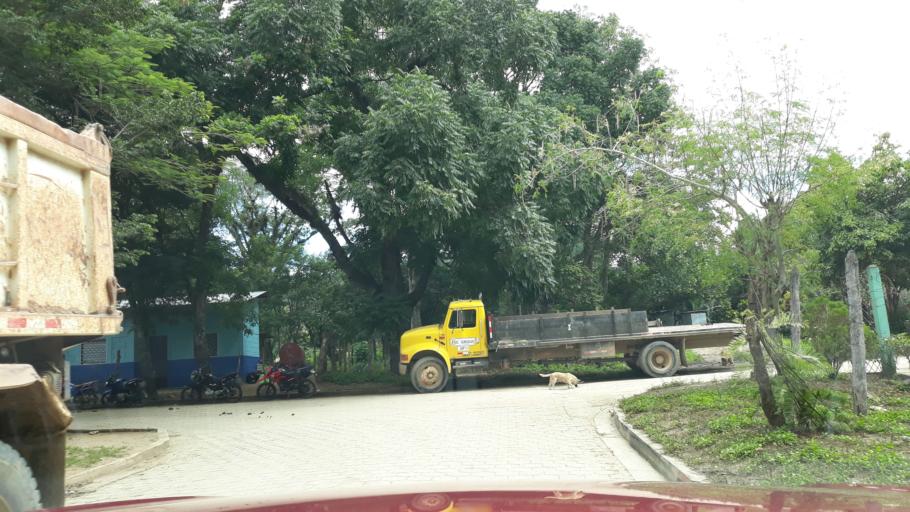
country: HN
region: El Paraiso
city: Santa Cruz
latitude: 13.7323
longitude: -86.6227
